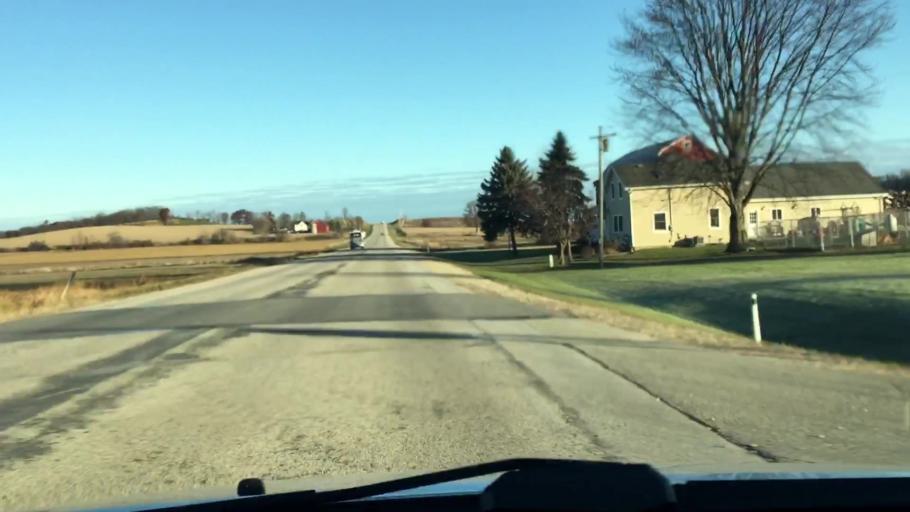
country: US
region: Wisconsin
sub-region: Dodge County
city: Theresa
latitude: 43.4715
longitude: -88.4501
